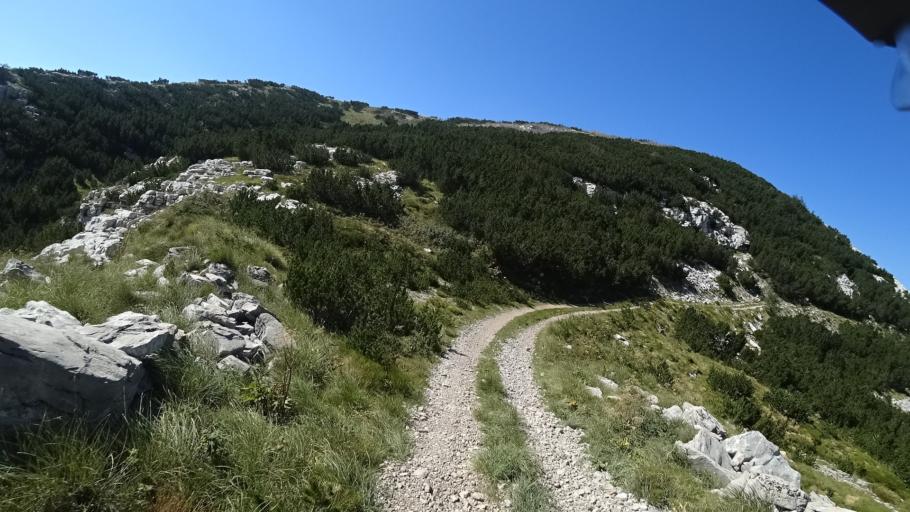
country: HR
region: Splitsko-Dalmatinska
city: Hrvace
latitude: 43.9338
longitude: 16.6005
